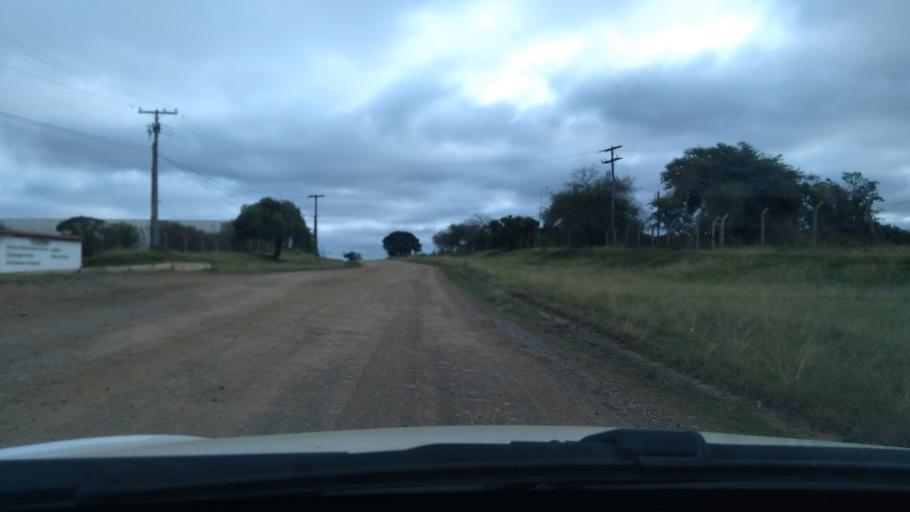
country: BR
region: Rio Grande do Sul
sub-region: Dom Pedrito
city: Dom Pedrito
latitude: -30.9833
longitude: -54.6418
